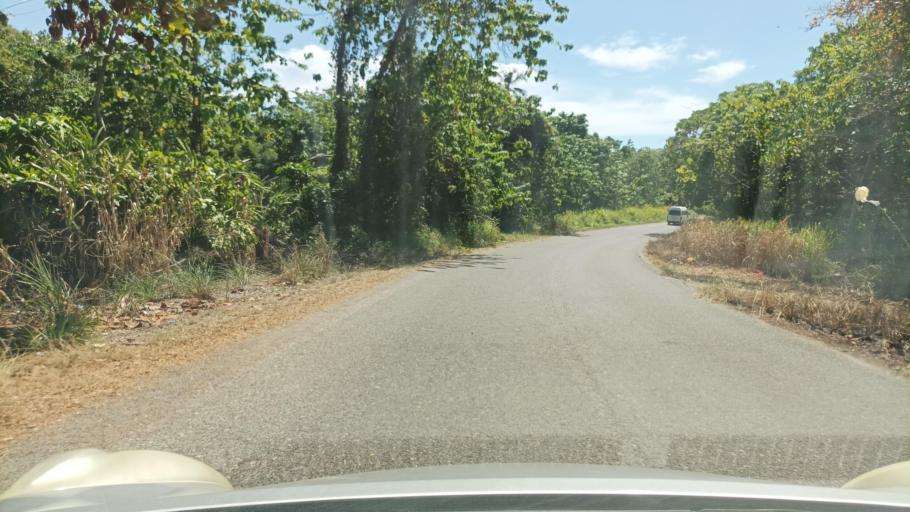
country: SB
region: Guadalcanal
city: Honiara
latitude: -9.3762
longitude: 159.8634
